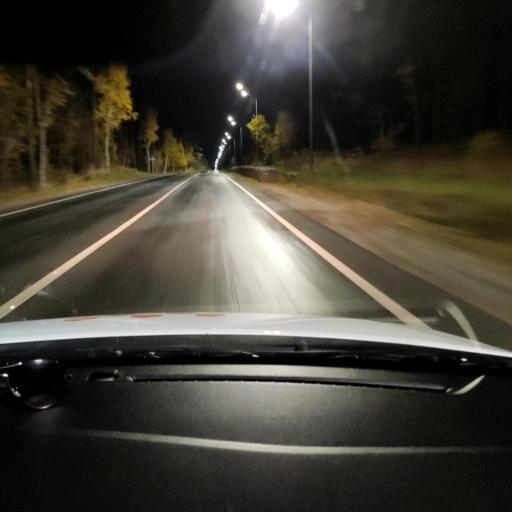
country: RU
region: Tatarstan
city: Verkhniy Uslon
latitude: 55.6394
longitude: 49.0310
